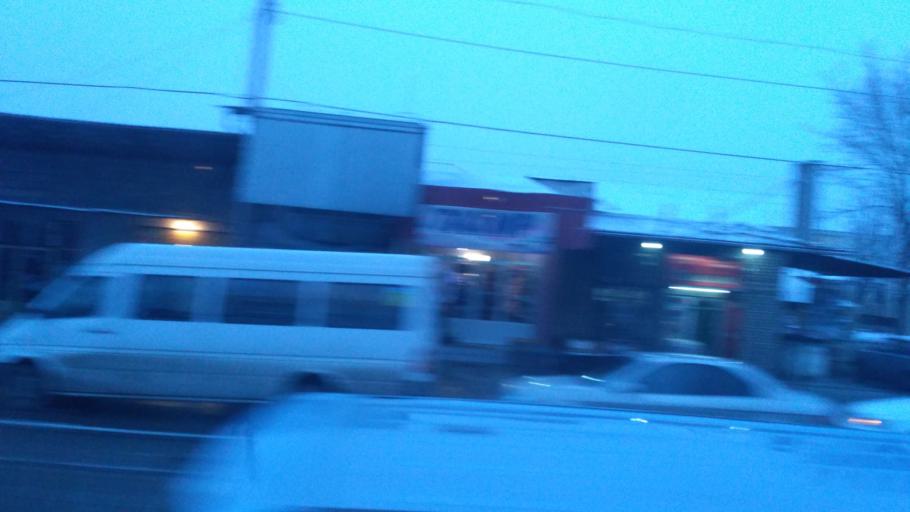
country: KZ
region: Ongtustik Qazaqstan
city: Shymkent
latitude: 42.3742
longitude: 69.5018
